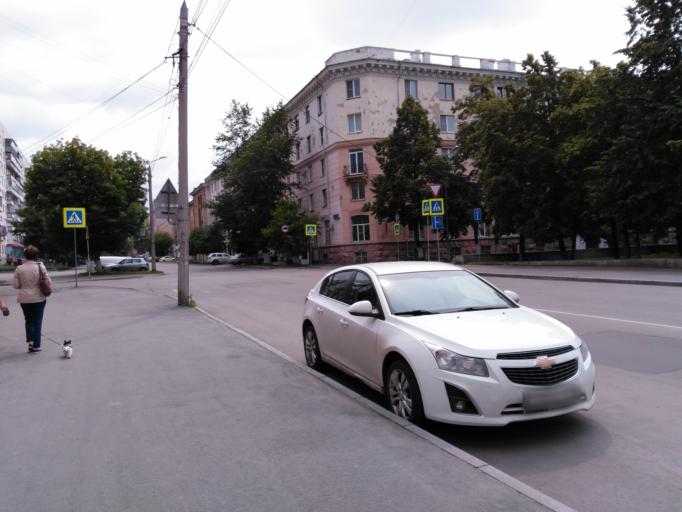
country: RU
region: Chelyabinsk
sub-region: Gorod Chelyabinsk
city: Chelyabinsk
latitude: 55.1633
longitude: 61.4066
